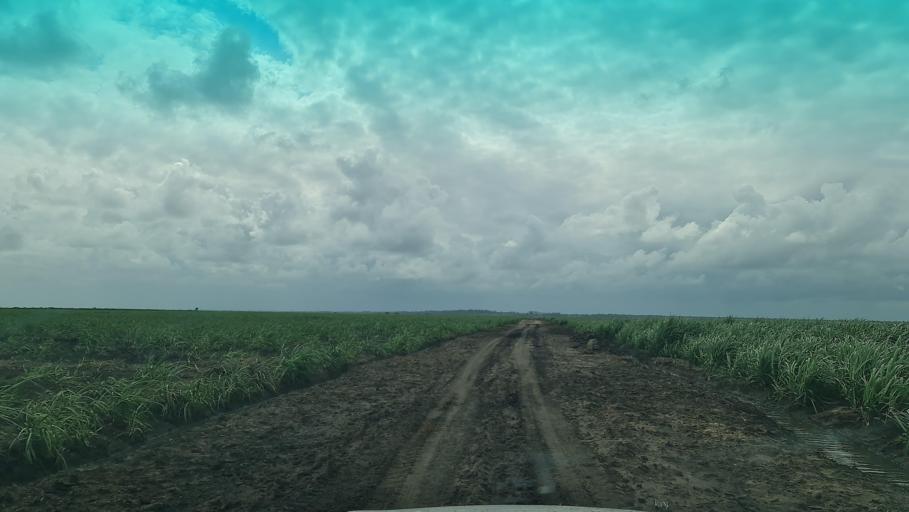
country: MZ
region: Maputo
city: Manhica
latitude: -25.4538
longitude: 32.8359
